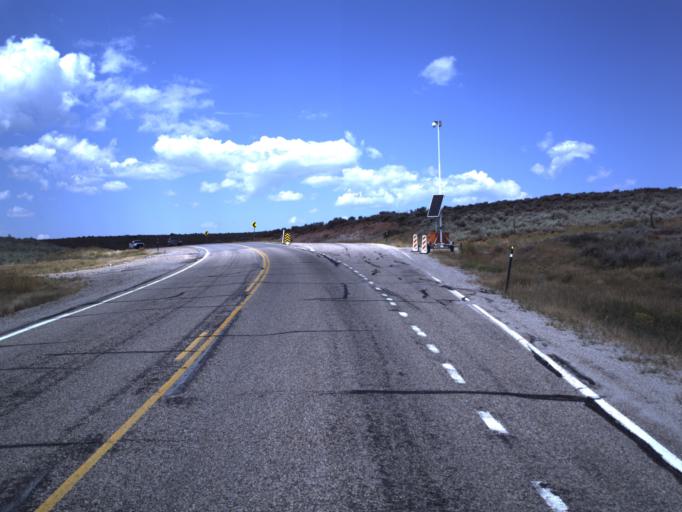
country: US
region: Utah
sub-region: Rich County
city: Randolph
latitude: 41.8068
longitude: -111.2493
